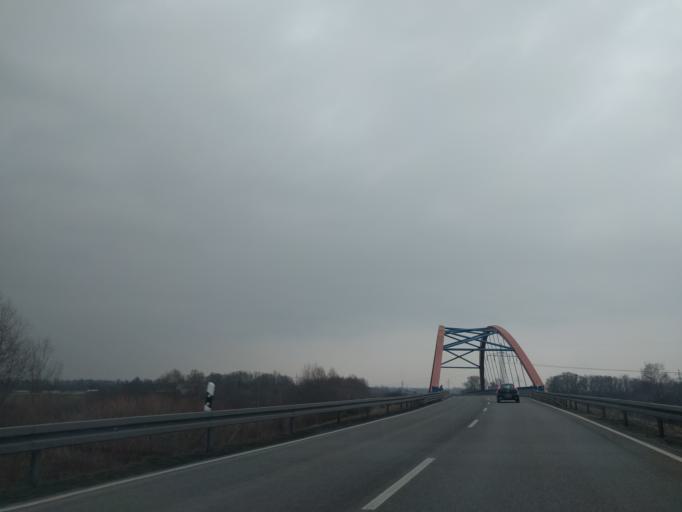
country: DE
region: Bavaria
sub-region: Swabia
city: Asbach-Baumenheim
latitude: 48.6936
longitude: 10.7989
